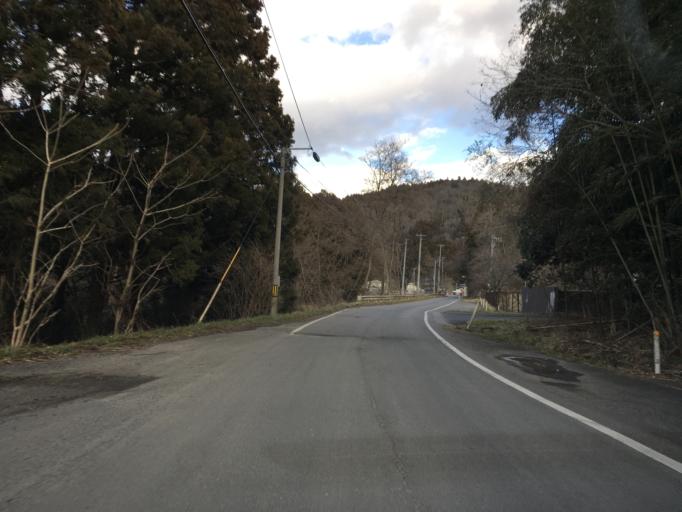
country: JP
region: Miyagi
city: Wakuya
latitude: 38.7129
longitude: 141.2977
